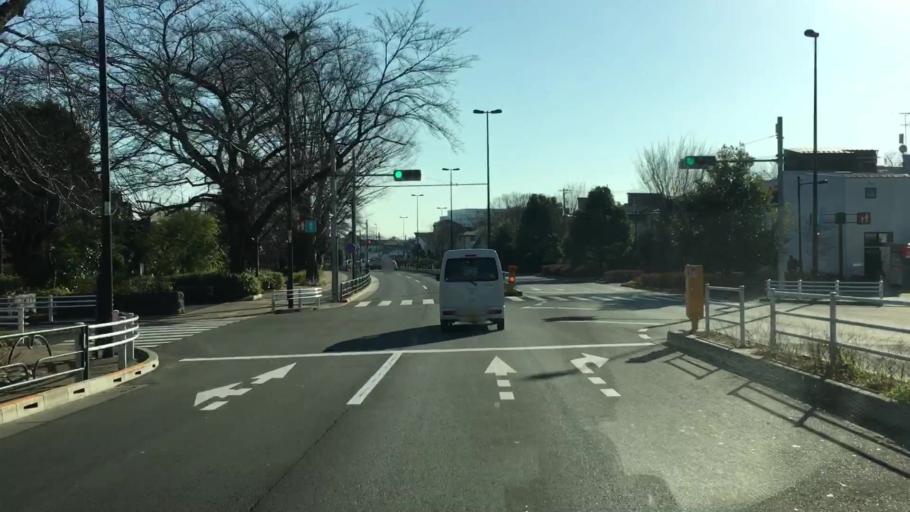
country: JP
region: Tokyo
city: Kamirenjaku
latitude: 35.7062
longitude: 139.5507
